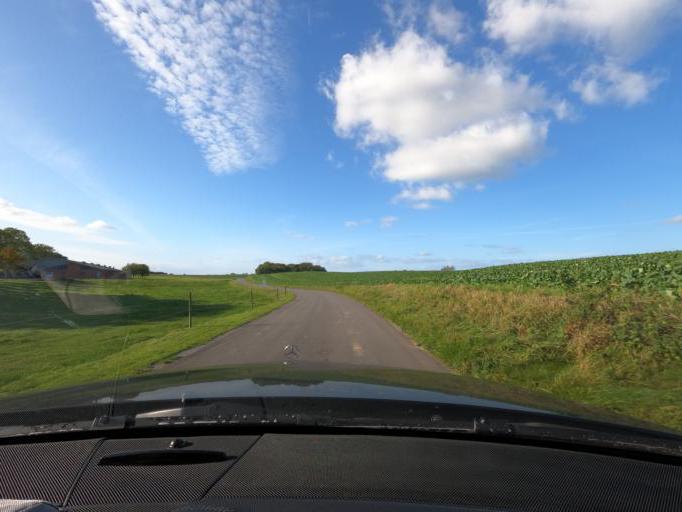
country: DK
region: South Denmark
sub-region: Sonderborg Kommune
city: Dybbol
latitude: 54.8833
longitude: 9.7220
